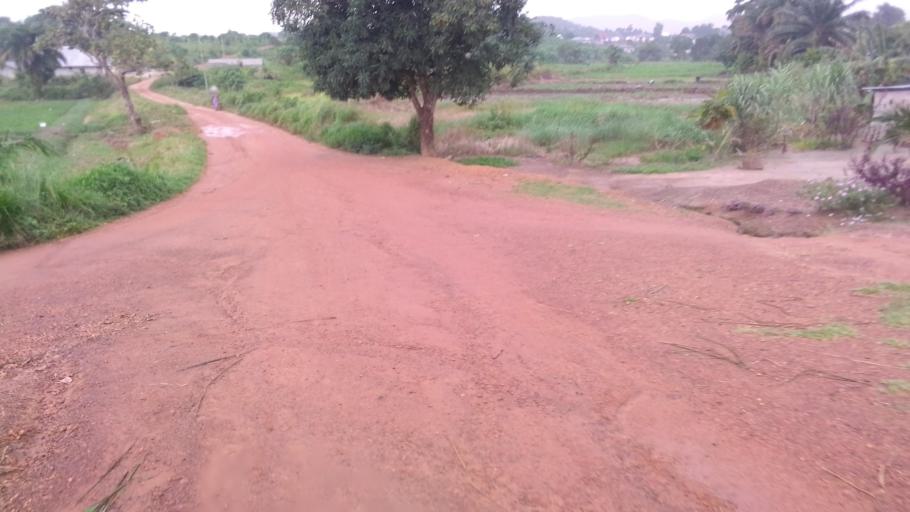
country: SL
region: Eastern Province
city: Kenema
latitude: 7.8410
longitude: -11.1780
